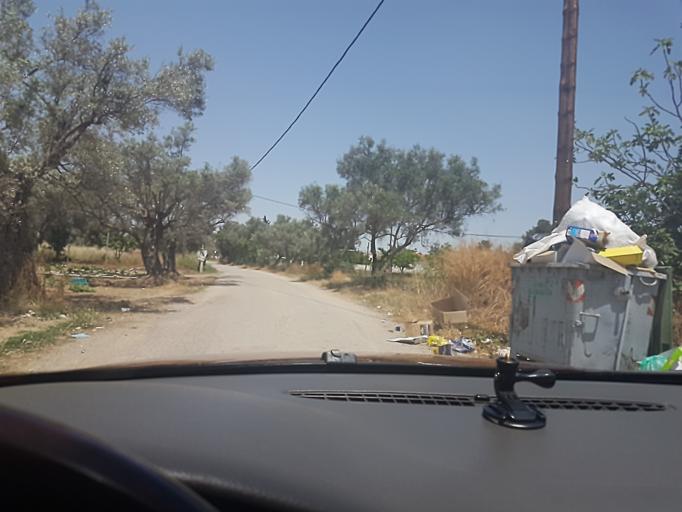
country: GR
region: Central Greece
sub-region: Nomos Evvoias
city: Vasilikon
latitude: 38.4139
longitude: 23.6686
